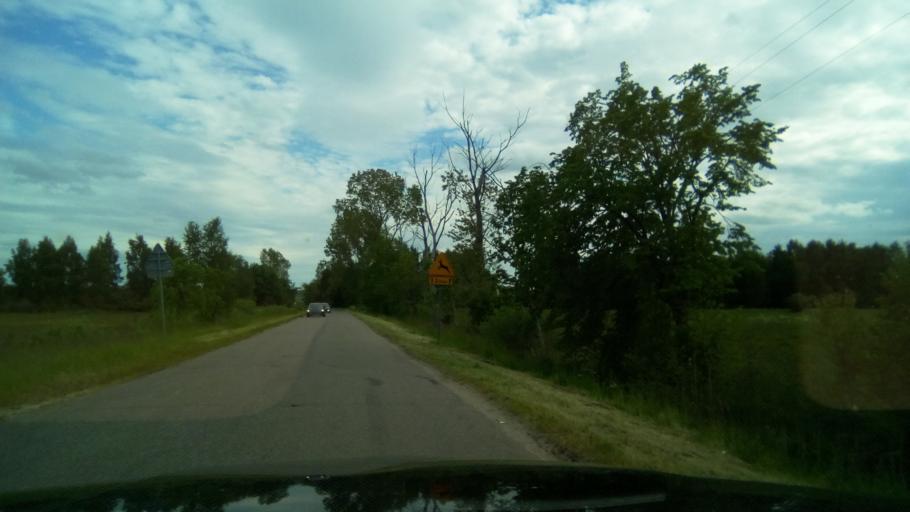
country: PL
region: Pomeranian Voivodeship
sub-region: Powiat pucki
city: Krokowa
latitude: 54.8216
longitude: 18.0870
